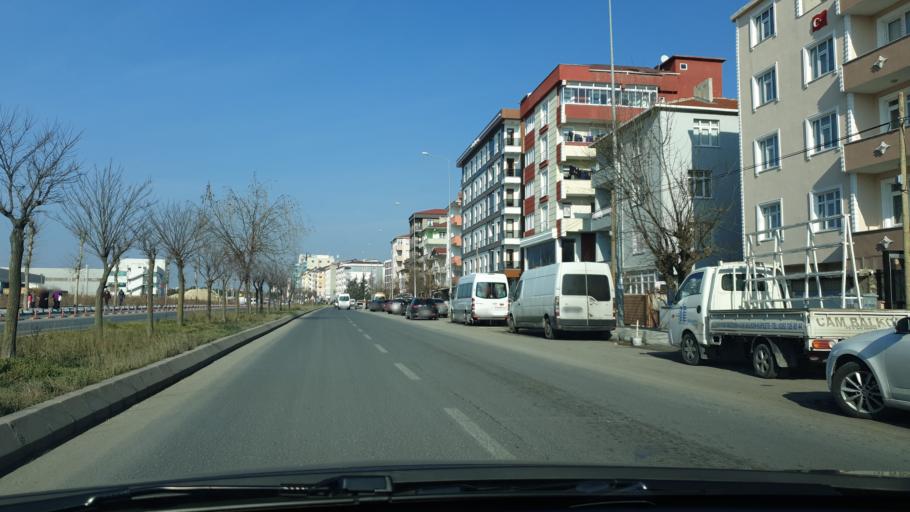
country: TR
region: Tekirdag
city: Cerkezkoey
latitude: 41.2894
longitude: 27.9917
